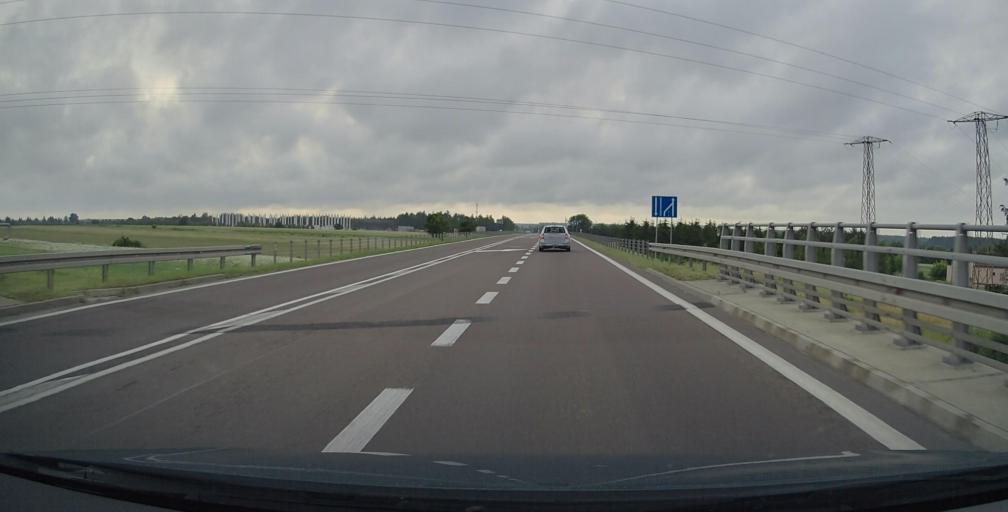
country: PL
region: Masovian Voivodeship
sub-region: Siedlce
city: Siedlce
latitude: 52.1316
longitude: 22.3065
